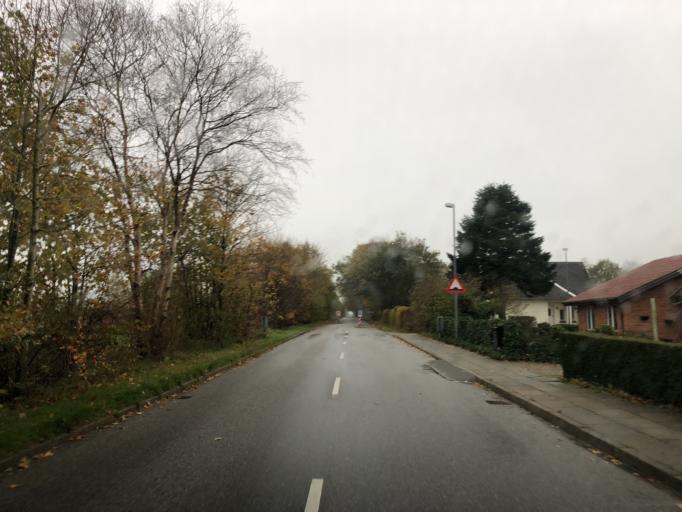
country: DK
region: Central Jutland
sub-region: Herning Kommune
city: Snejbjerg
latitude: 56.0910
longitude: 8.9115
